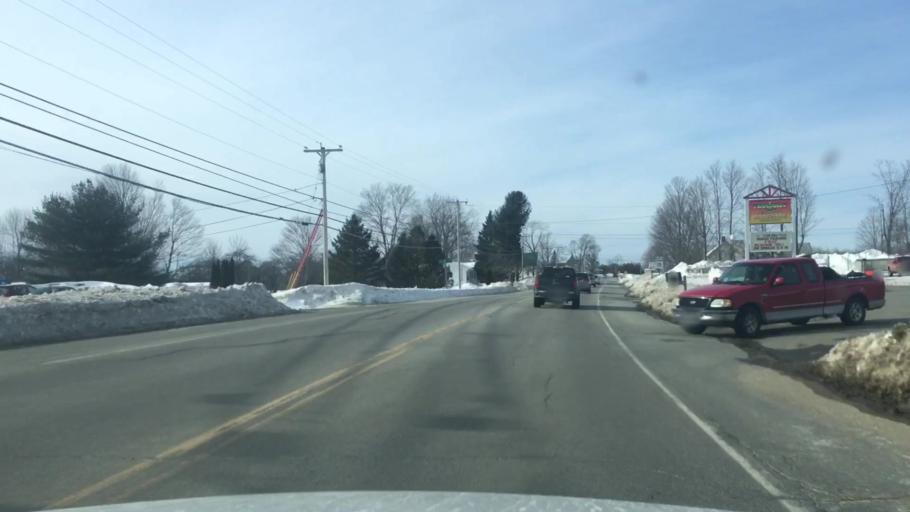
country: US
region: Maine
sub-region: Penobscot County
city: Charleston
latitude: 44.9894
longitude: -69.0144
